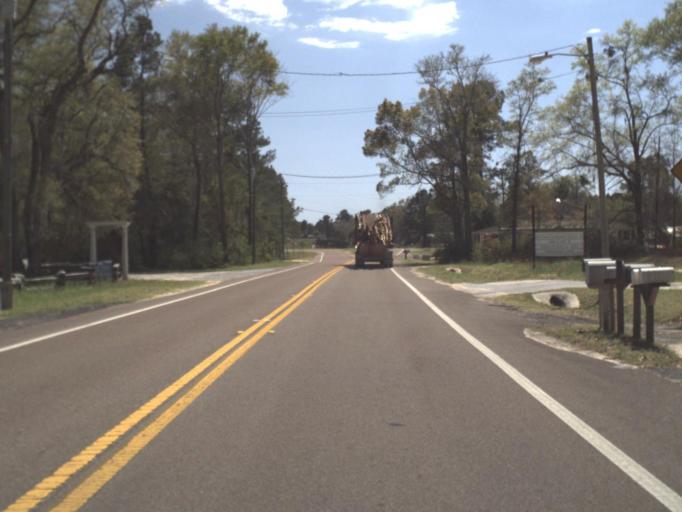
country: US
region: Florida
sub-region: Walton County
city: DeFuniak Springs
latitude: 30.7191
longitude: -85.9360
